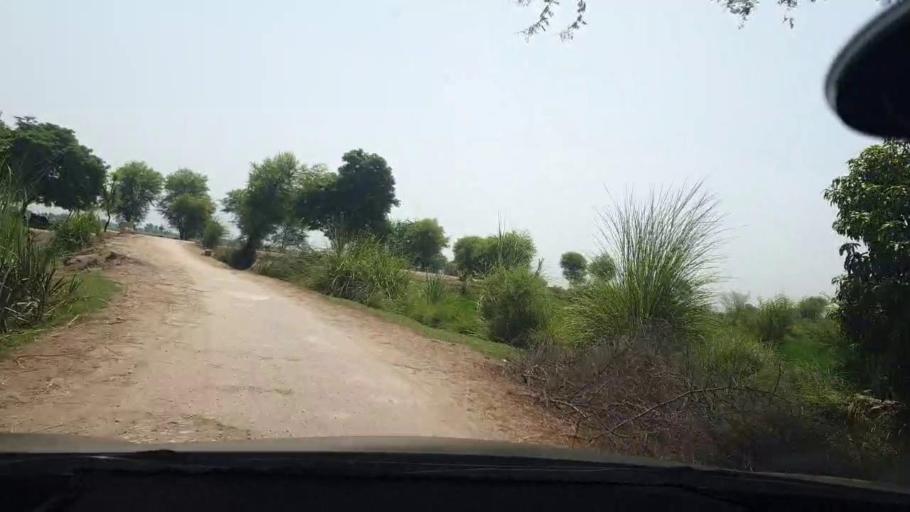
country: PK
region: Sindh
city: Kambar
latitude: 27.6645
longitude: 67.9449
